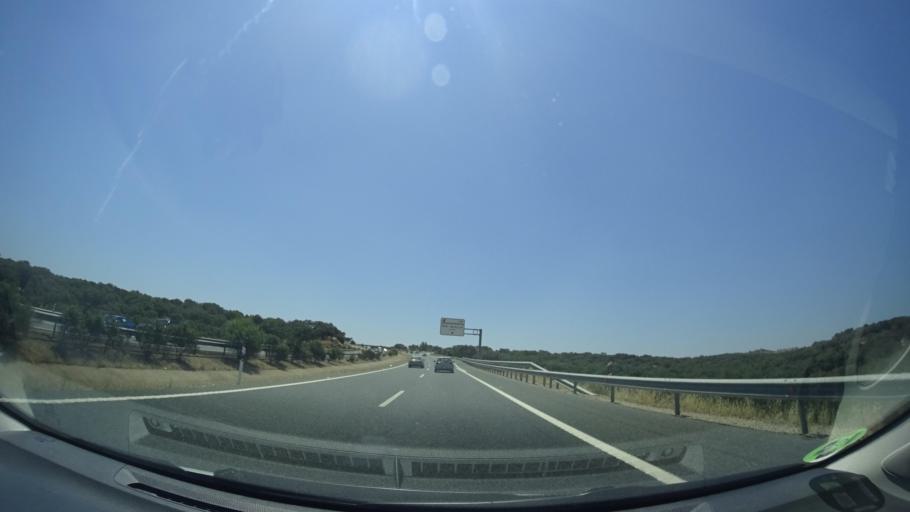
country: ES
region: Andalusia
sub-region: Provincia de Huelva
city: Santa Olalla del Cala
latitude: 37.9233
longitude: -6.2271
